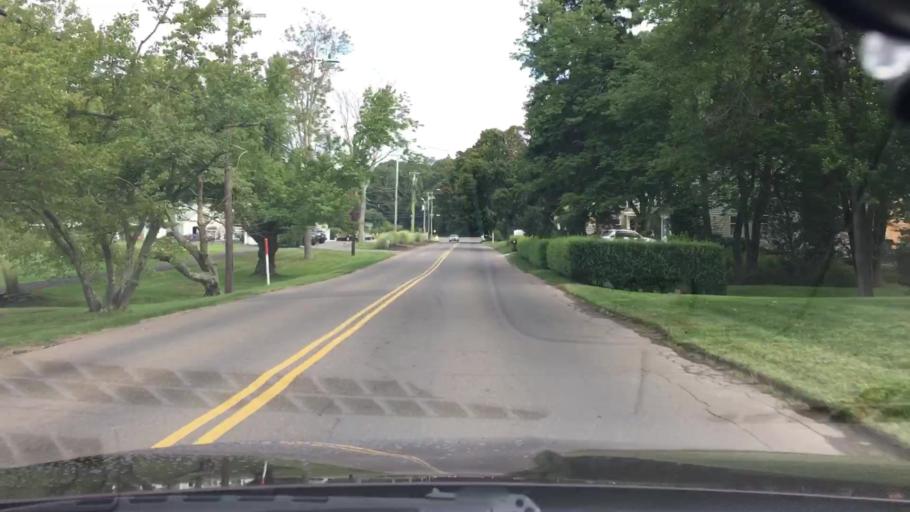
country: US
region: Connecticut
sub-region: New Haven County
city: Madison Center
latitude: 41.2749
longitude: -72.6076
